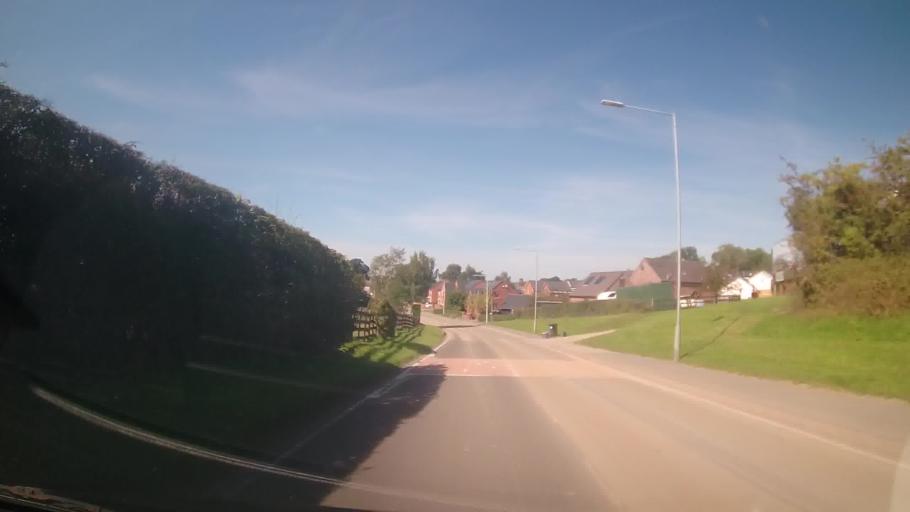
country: GB
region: England
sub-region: Shropshire
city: Mainstone
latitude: 52.5381
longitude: -3.0691
